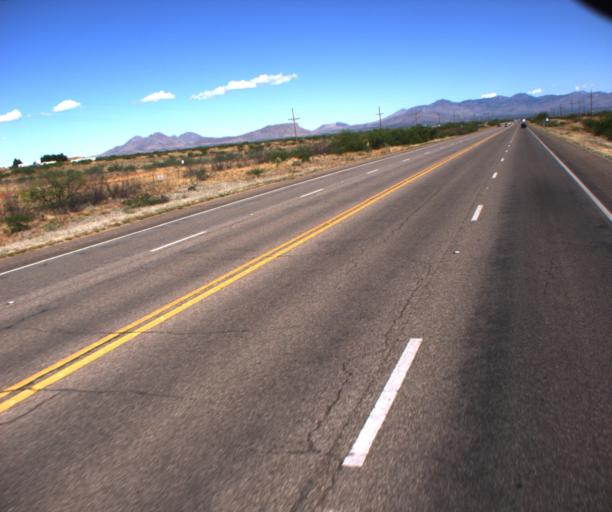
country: US
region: Arizona
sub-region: Cochise County
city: Sierra Vista
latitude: 31.5883
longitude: -110.3218
